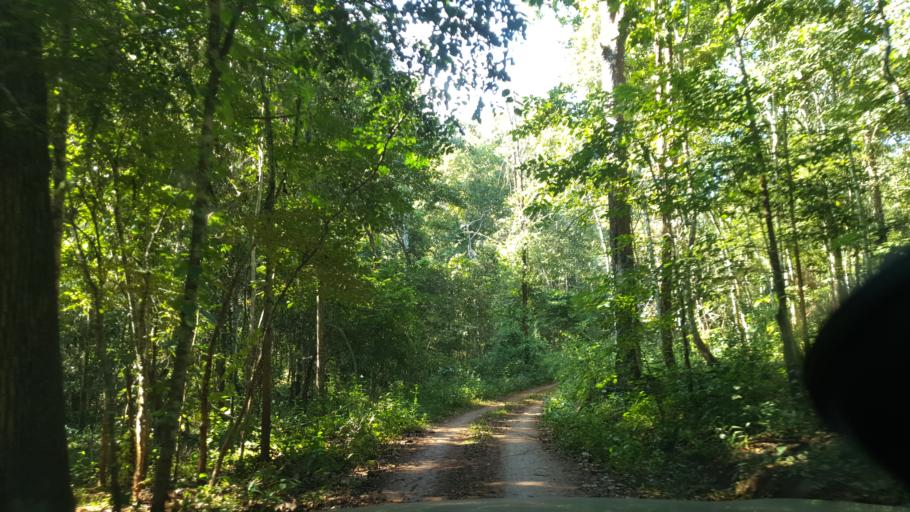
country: TH
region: Chiang Mai
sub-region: Amphoe Chiang Dao
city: Chiang Dao
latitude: 19.3202
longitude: 98.7261
